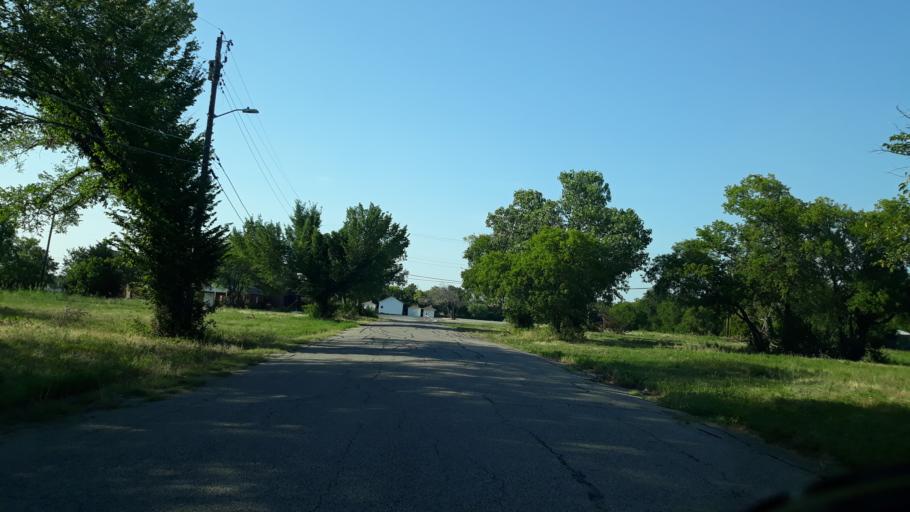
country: US
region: Texas
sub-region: Tarrant County
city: Euless
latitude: 32.8491
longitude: -97.0148
